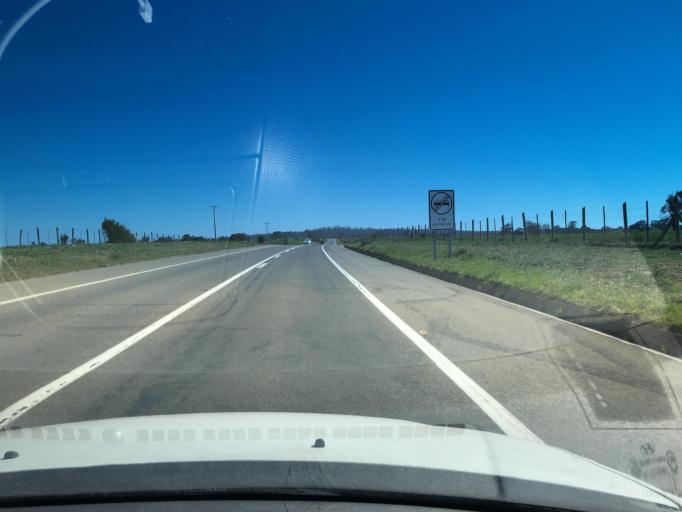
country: CL
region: Valparaiso
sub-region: San Antonio Province
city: El Tabo
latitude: -33.4064
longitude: -71.5329
